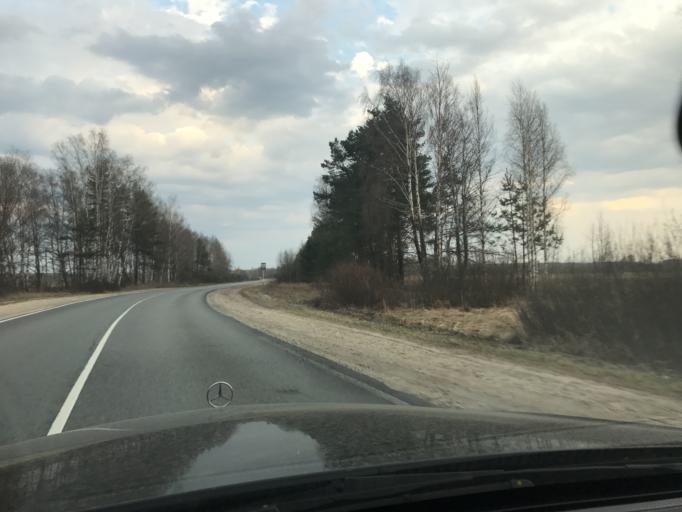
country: RU
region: Vladimir
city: Murom
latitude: 55.6327
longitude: 41.8773
